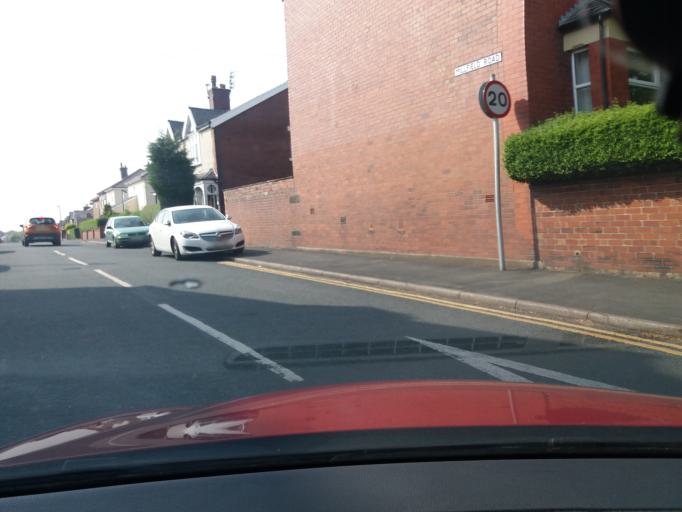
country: GB
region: England
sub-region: Lancashire
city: Chorley
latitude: 53.6580
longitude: -2.6319
